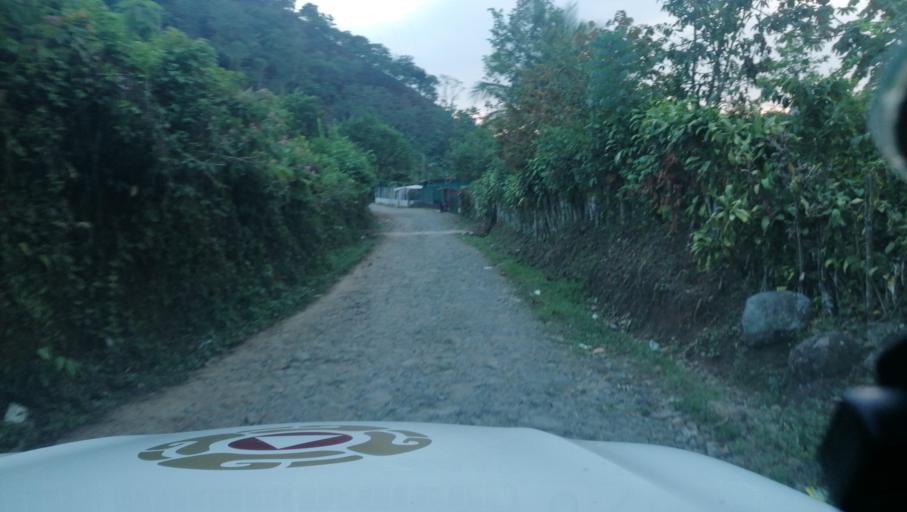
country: MX
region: Chiapas
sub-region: Cacahoatan
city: Benito Juarez
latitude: 15.0705
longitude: -92.2316
